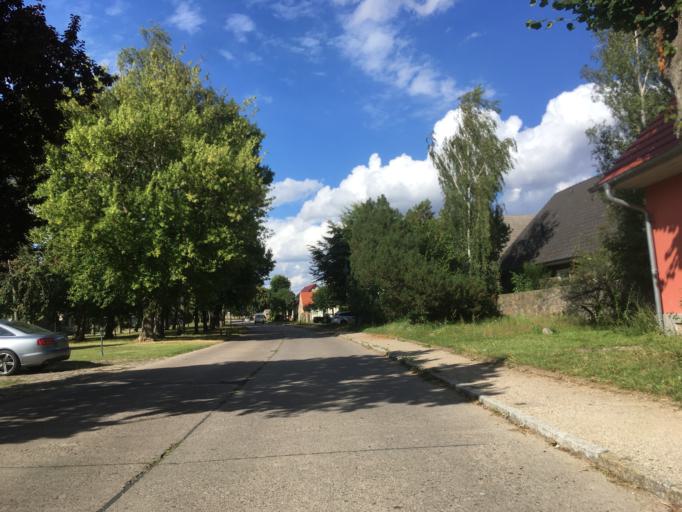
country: DE
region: Brandenburg
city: Liepe
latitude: 52.9129
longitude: 13.9622
